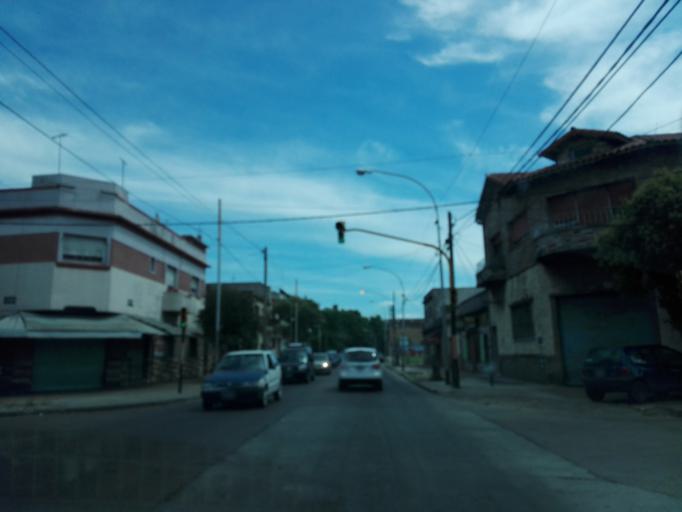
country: AR
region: Buenos Aires
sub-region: Partido de Avellaneda
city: Avellaneda
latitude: -34.6951
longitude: -58.3586
